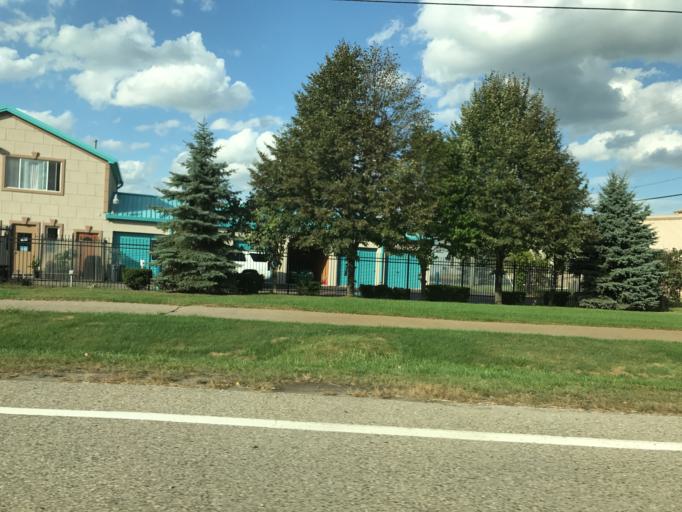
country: US
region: Michigan
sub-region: Oakland County
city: Wixom
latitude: 42.4998
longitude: -83.5606
